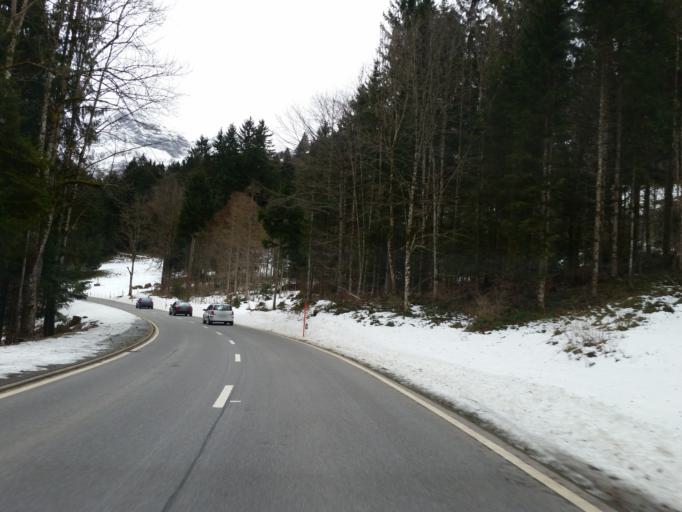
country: CH
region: Appenzell Ausserrhoden
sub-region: Bezirk Hinterland
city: Urnasch
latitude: 47.2774
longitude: 9.2811
